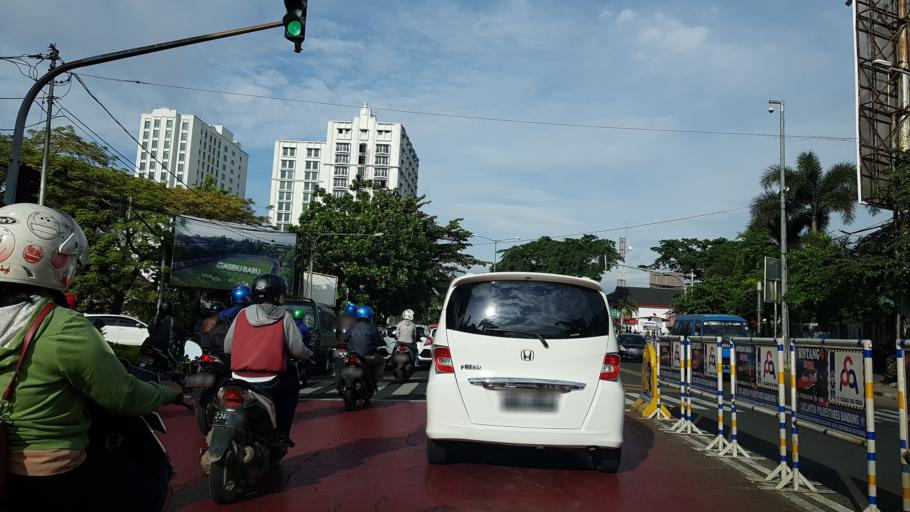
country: ID
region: West Java
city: Bandung
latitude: -6.8993
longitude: 107.6196
